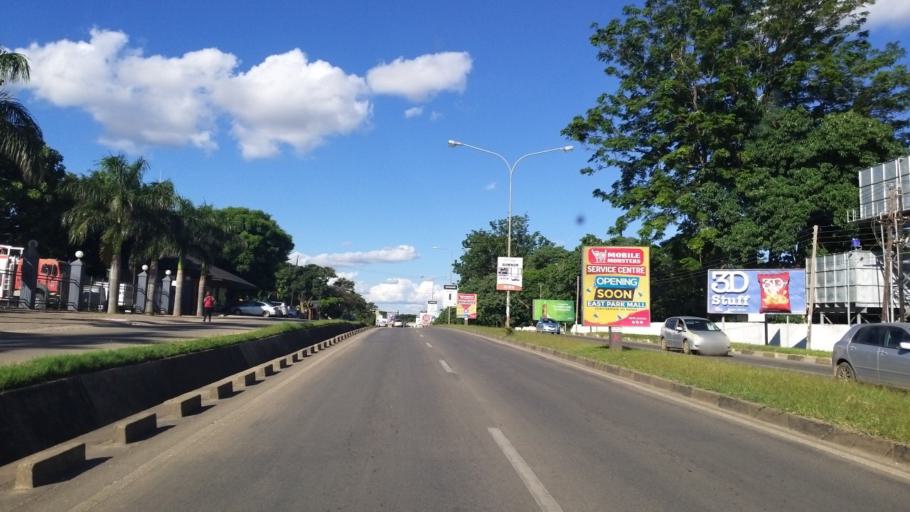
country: ZM
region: Lusaka
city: Lusaka
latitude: -15.3953
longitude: 28.3115
